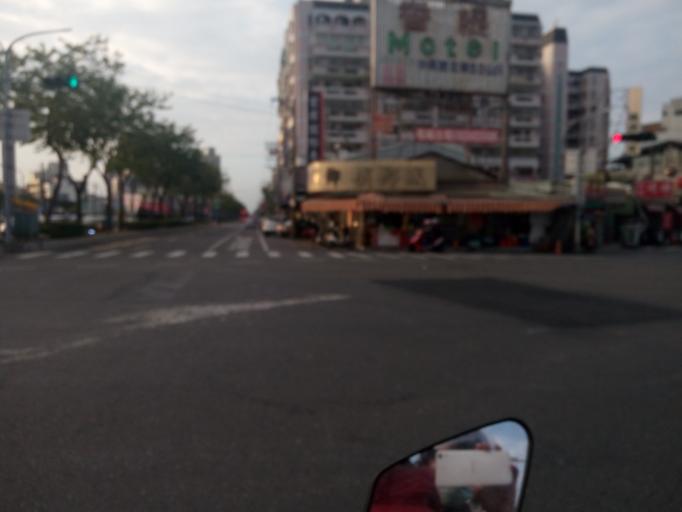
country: TW
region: Taiwan
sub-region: Chiayi
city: Jiayi Shi
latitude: 23.4777
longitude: 120.4343
